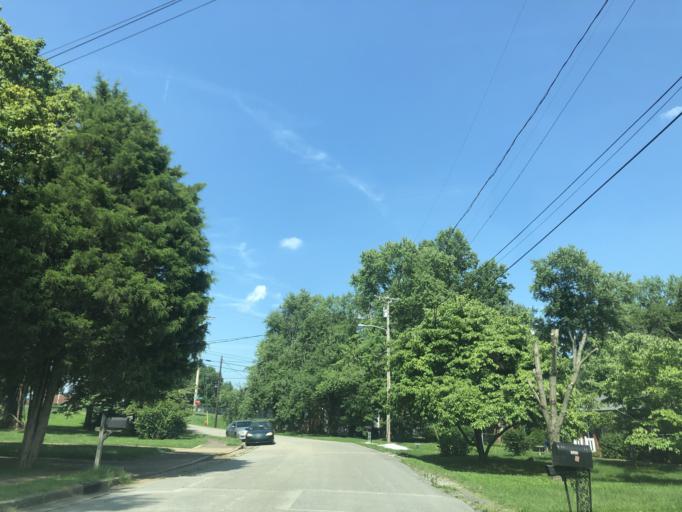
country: US
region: Tennessee
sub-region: Davidson County
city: Lakewood
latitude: 36.1655
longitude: -86.6548
